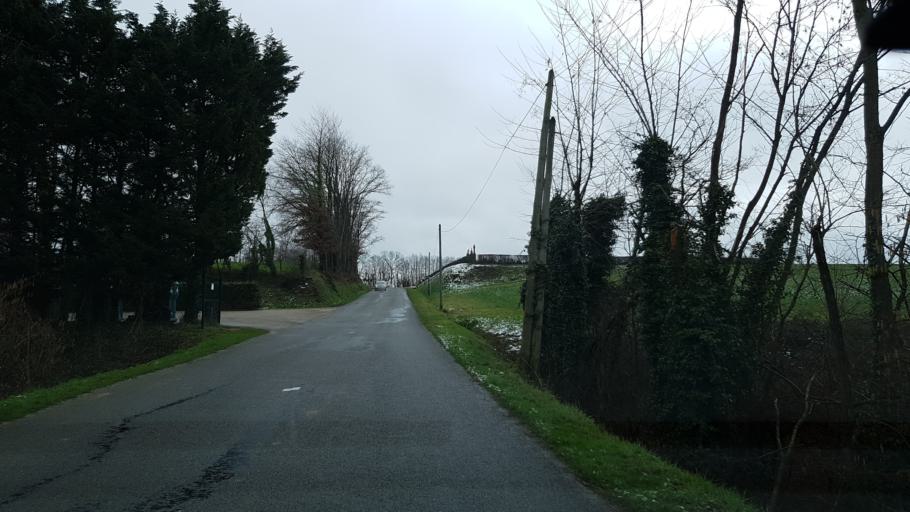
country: FR
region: Rhone-Alpes
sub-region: Departement de l'Ain
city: Buellas
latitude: 46.1974
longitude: 5.1246
